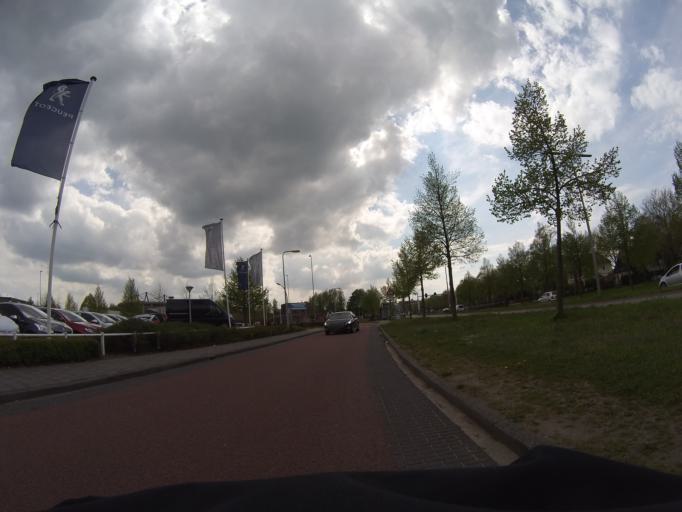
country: NL
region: Overijssel
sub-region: Gemeente Zwolle
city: Zwolle
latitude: 52.5061
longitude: 6.0786
